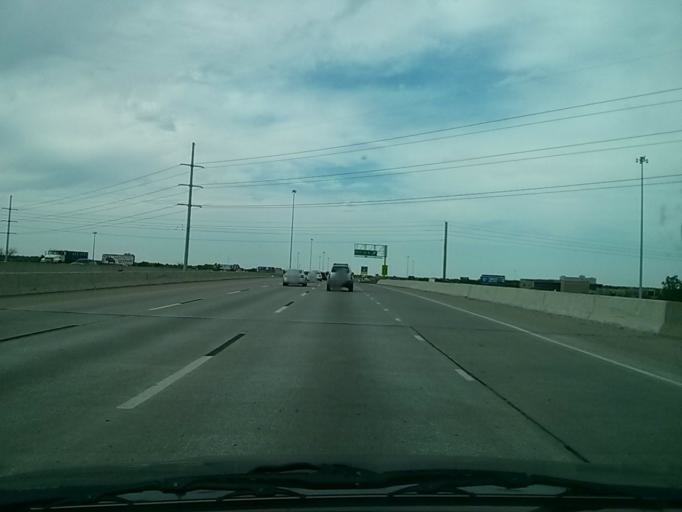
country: US
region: Oklahoma
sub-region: Tulsa County
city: Broken Arrow
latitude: 36.0893
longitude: -95.8585
